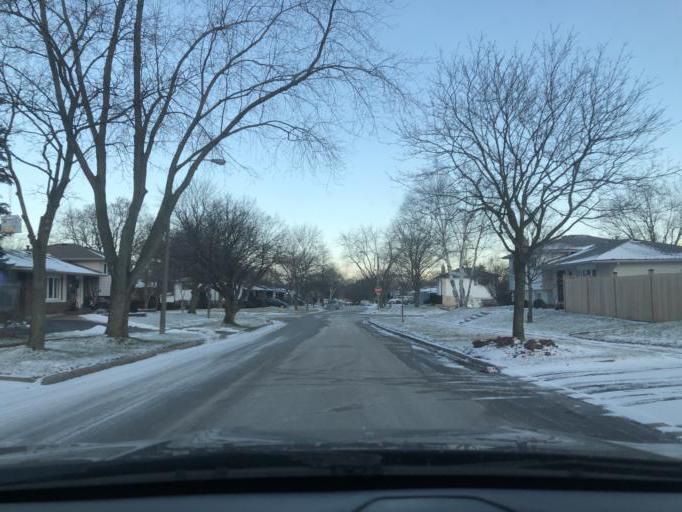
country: CA
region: Ontario
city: Pickering
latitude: 43.7880
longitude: -79.1444
